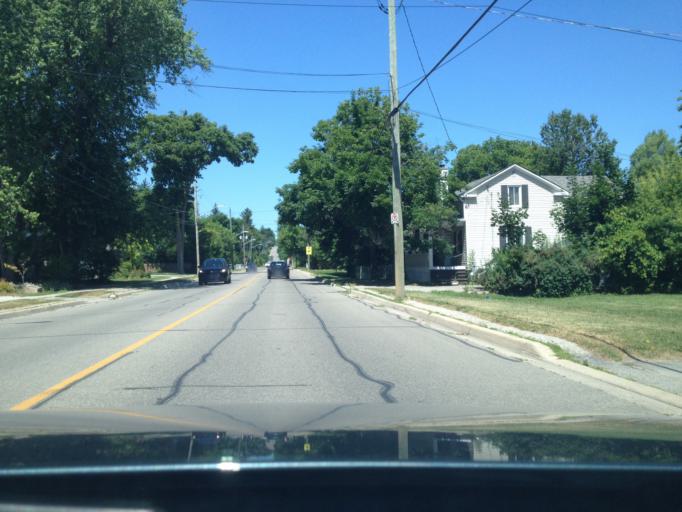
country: CA
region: Ontario
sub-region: Halton
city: Milton
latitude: 43.6664
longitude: -79.9249
